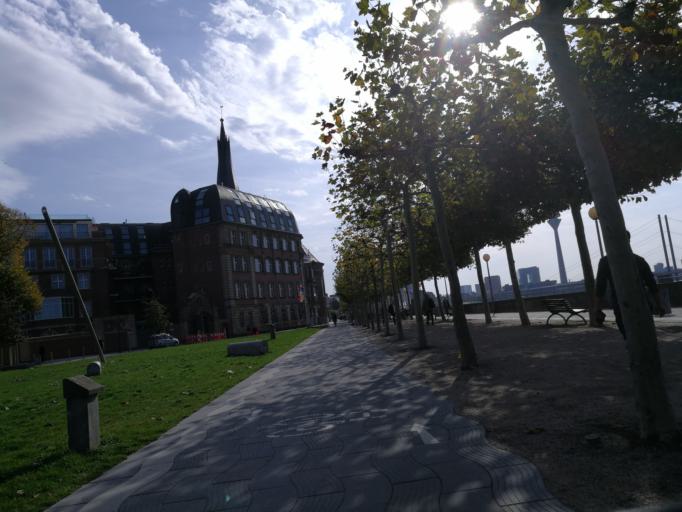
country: DE
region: North Rhine-Westphalia
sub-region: Regierungsbezirk Dusseldorf
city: Dusseldorf
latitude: 51.2297
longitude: 6.7711
